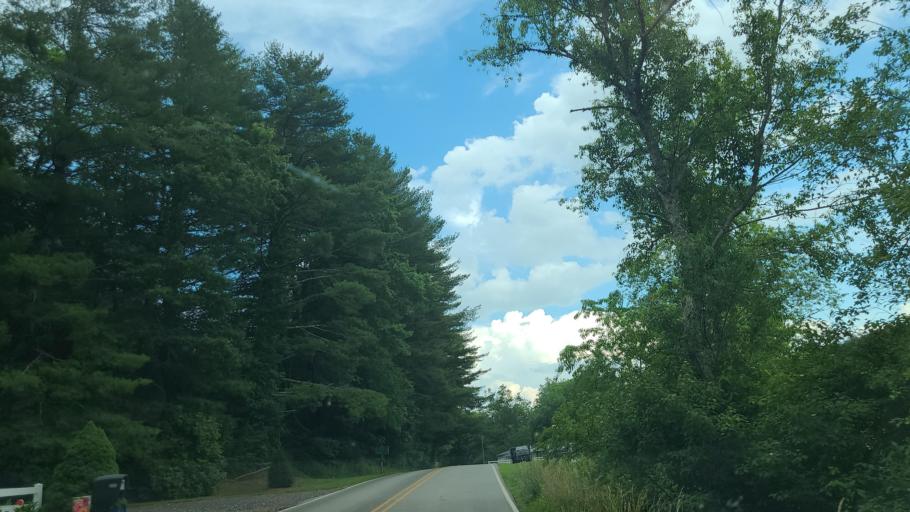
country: US
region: North Carolina
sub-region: Alleghany County
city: Sparta
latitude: 36.4162
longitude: -81.2666
